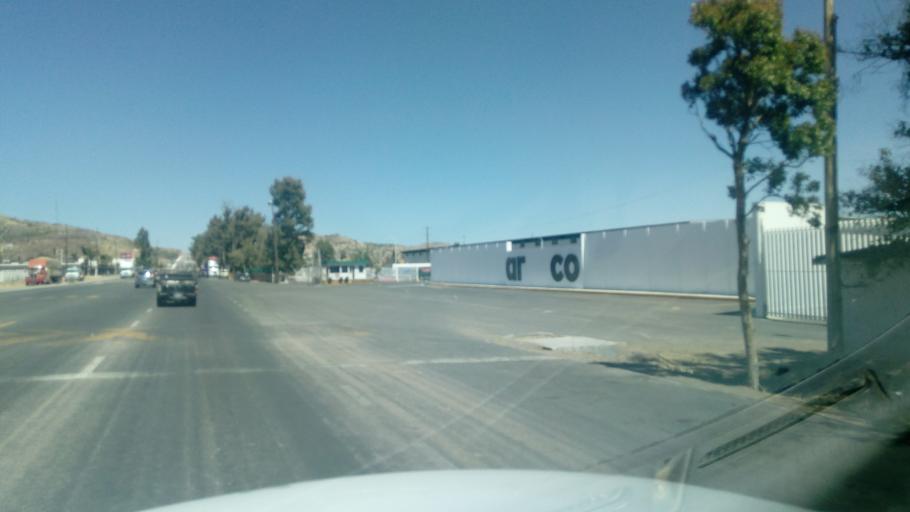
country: MX
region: Durango
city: Victoria de Durango
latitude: 24.0777
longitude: -104.6656
